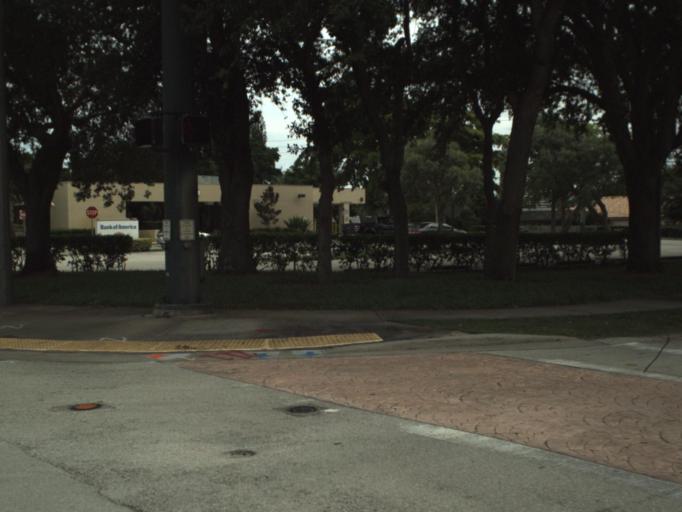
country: US
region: Florida
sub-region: Palm Beach County
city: Lake Park
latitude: 26.8213
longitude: -80.0592
